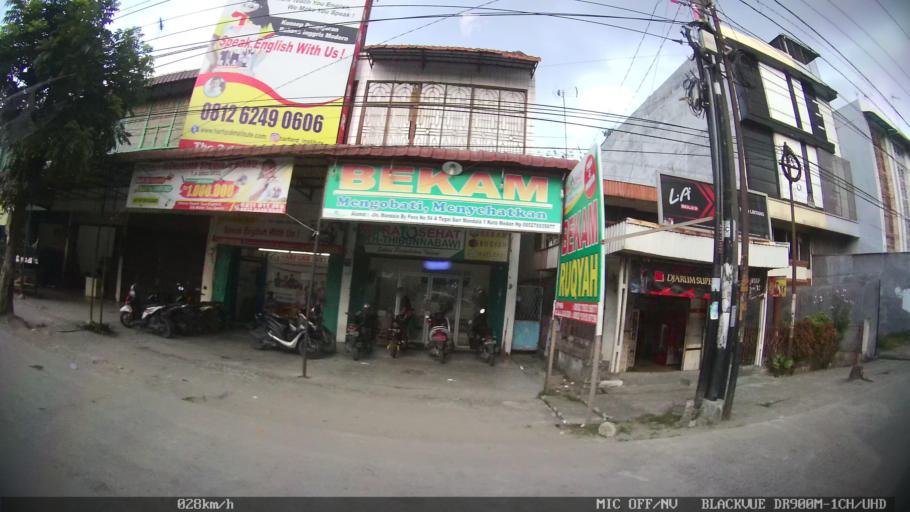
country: ID
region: North Sumatra
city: Medan
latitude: 3.5854
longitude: 98.7113
